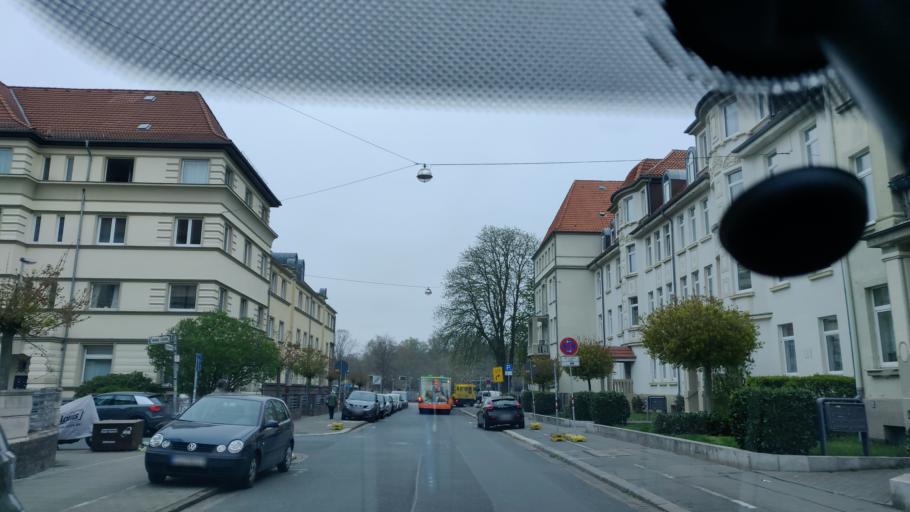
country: DE
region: Lower Saxony
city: Laatzen
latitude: 52.3342
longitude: 9.7925
